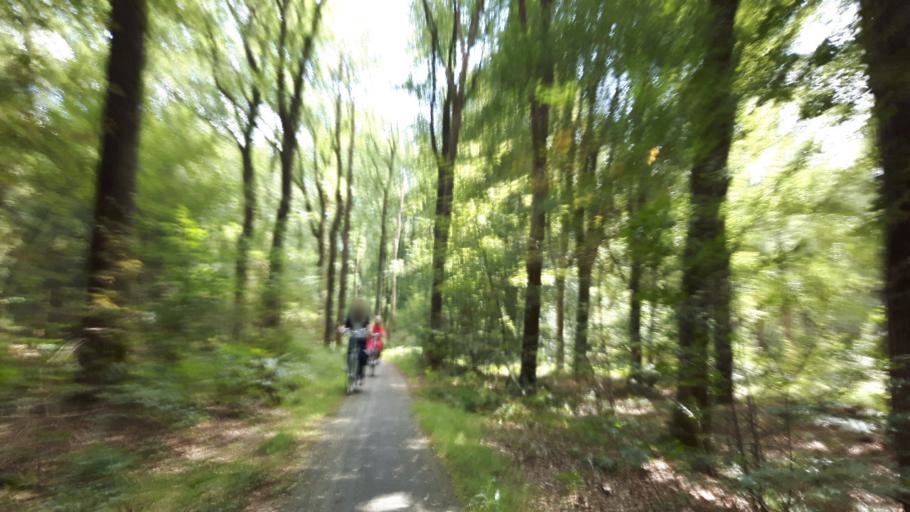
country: NL
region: Friesland
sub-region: Gemeente Smallingerland
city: Drachtstercompagnie
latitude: 53.0699
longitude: 6.2046
